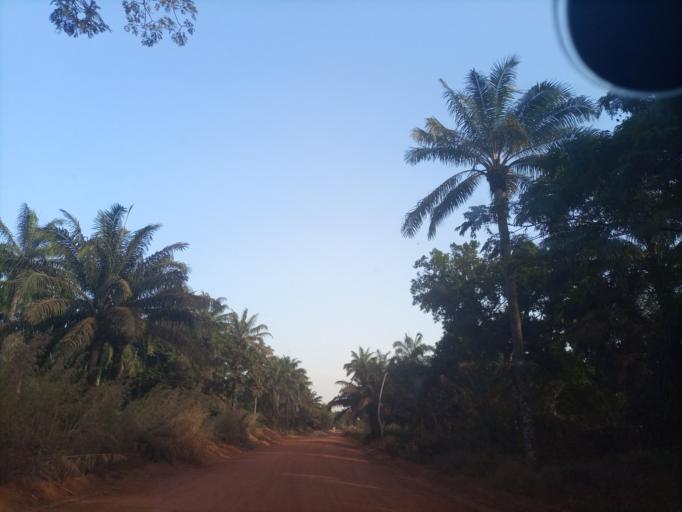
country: NG
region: Enugu
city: Obolo-Eke (1)
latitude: 6.7893
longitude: 7.5903
